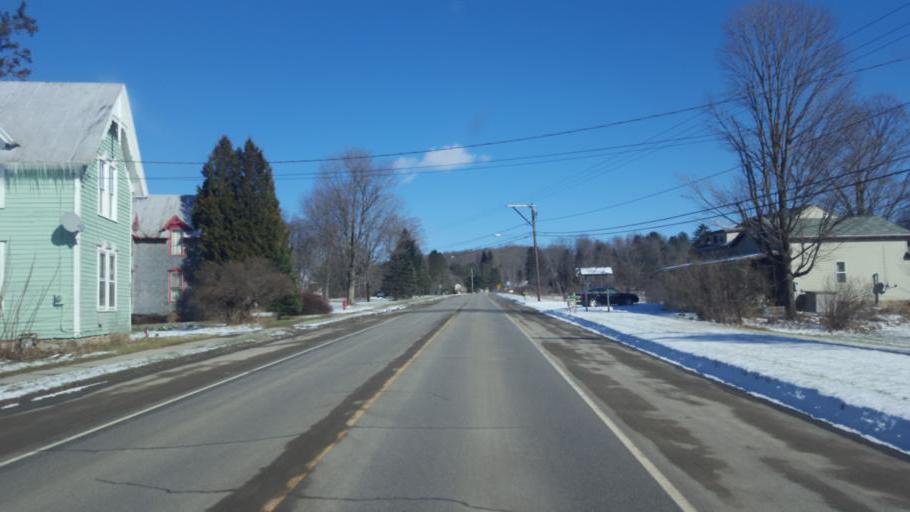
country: US
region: New York
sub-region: Allegany County
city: Friendship
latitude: 42.2064
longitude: -78.1276
